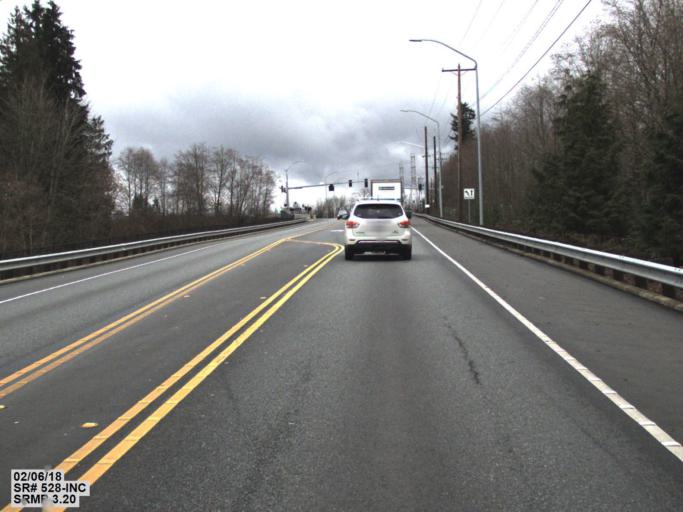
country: US
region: Washington
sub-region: Snohomish County
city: Marysville
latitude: 48.0535
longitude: -122.1165
